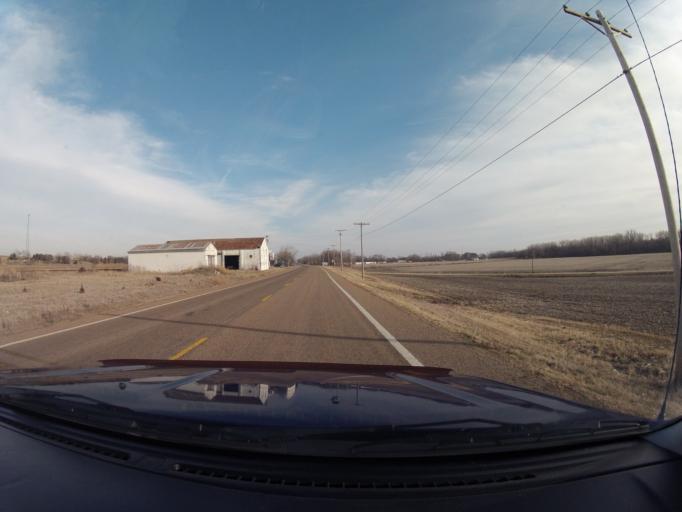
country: US
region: Kansas
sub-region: Pottawatomie County
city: Saint Marys
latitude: 39.1995
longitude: -96.0853
